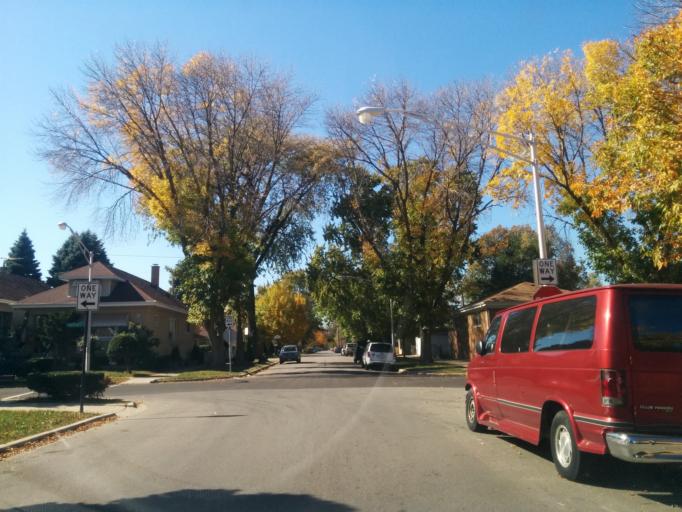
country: US
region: Illinois
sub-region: Cook County
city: Harwood Heights
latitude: 41.9439
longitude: -87.7880
